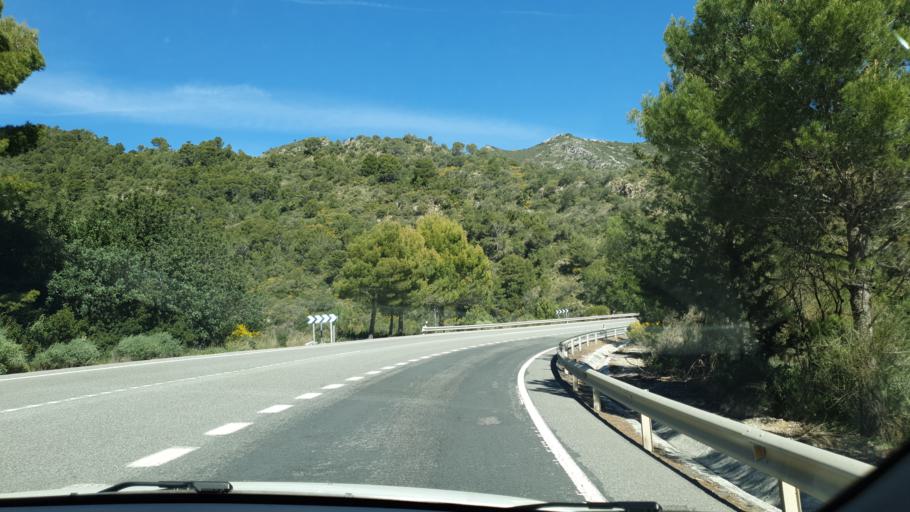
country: ES
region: Andalusia
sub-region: Provincia de Malaga
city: Ojen
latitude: 36.5672
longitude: -4.8648
